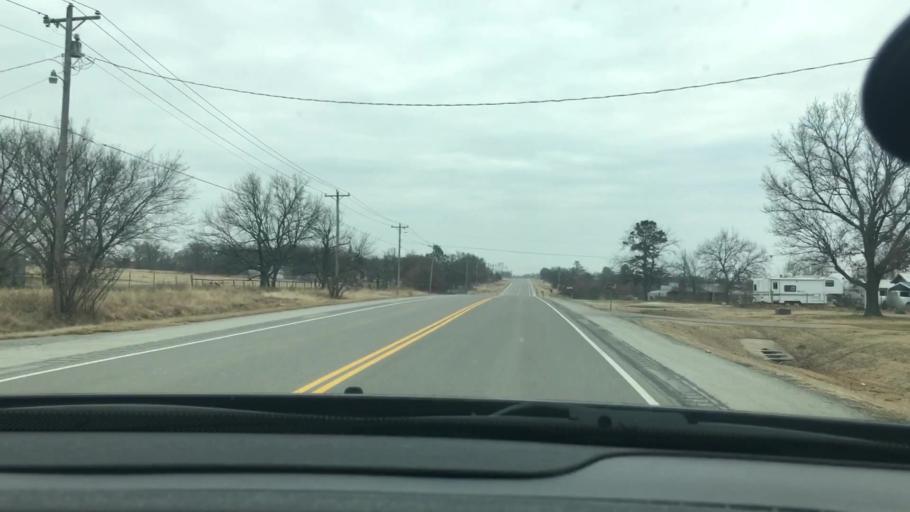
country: US
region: Oklahoma
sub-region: Carter County
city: Healdton
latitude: 34.4035
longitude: -97.5079
